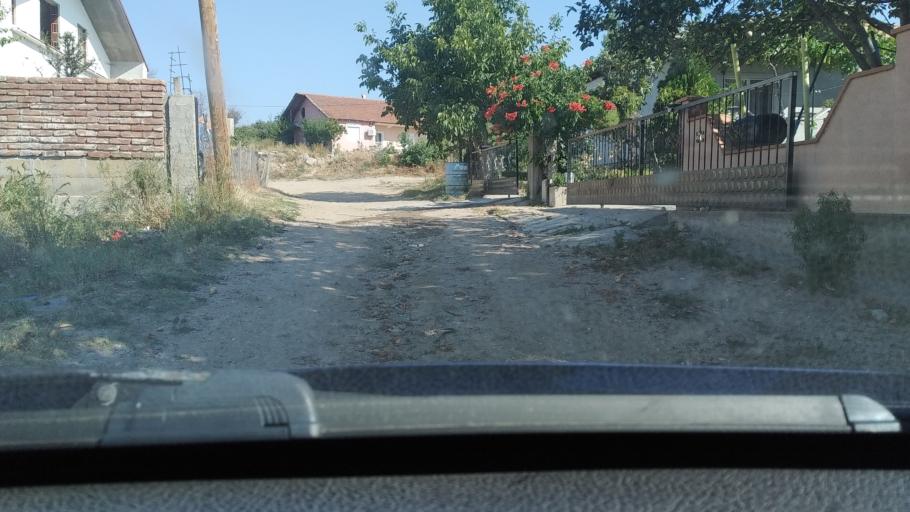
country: MK
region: Bogdanci
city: Bogdanci
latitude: 41.2053
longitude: 22.5670
